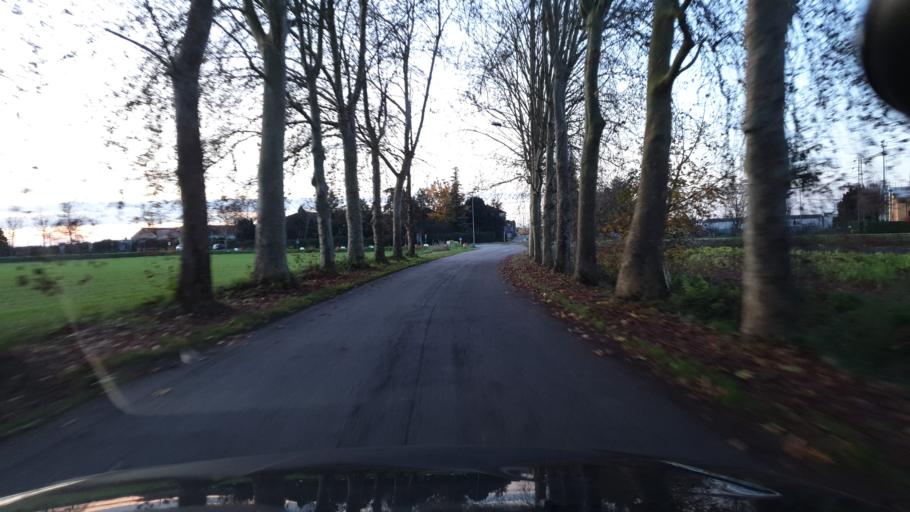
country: IT
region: Veneto
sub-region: Provincia di Rovigo
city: Fratta Polesine
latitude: 45.0288
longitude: 11.6399
